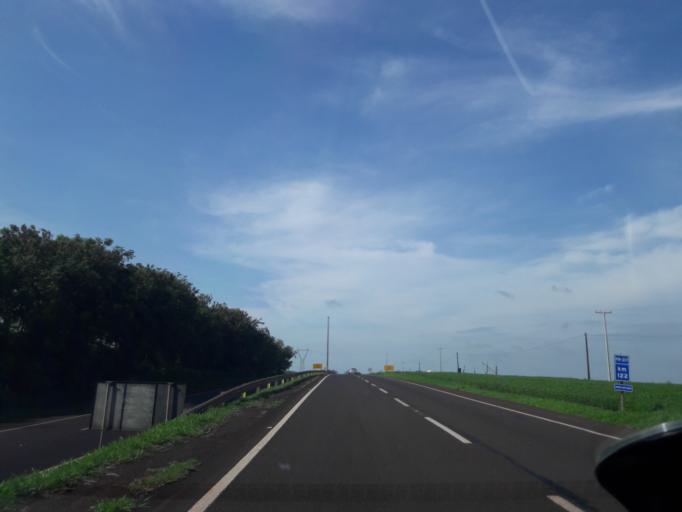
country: BR
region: Parana
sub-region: Paicandu
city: Paicandu
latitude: -23.5987
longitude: -52.0794
